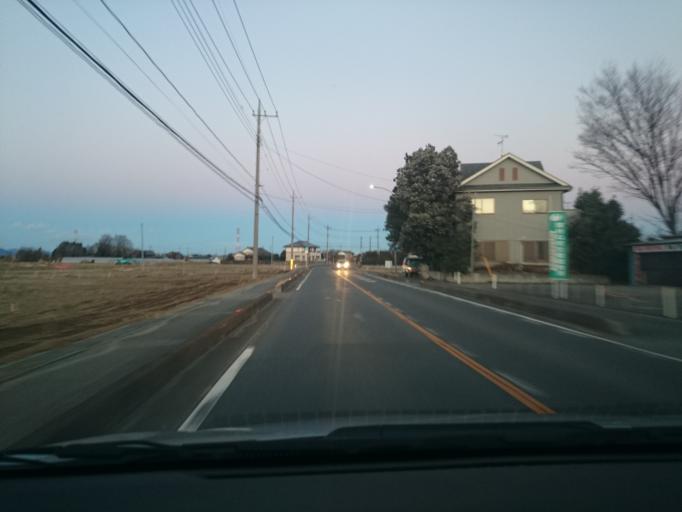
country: JP
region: Saitama
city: Fukayacho
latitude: 36.2272
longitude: 139.3285
